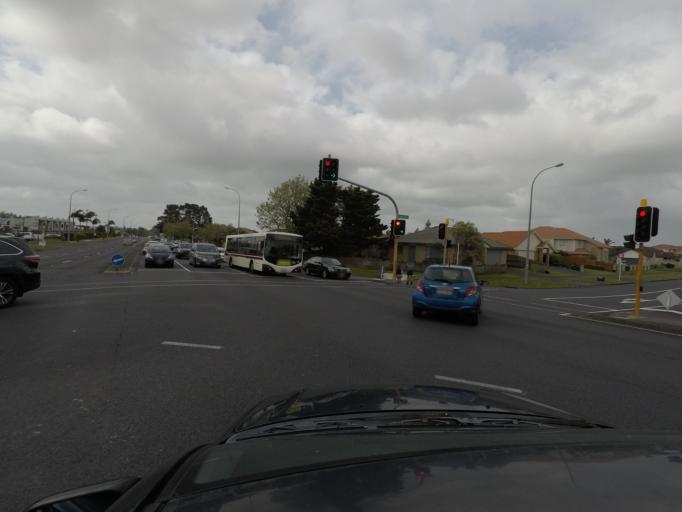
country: NZ
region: Auckland
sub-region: Auckland
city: Pakuranga
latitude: -36.9263
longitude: 174.9131
